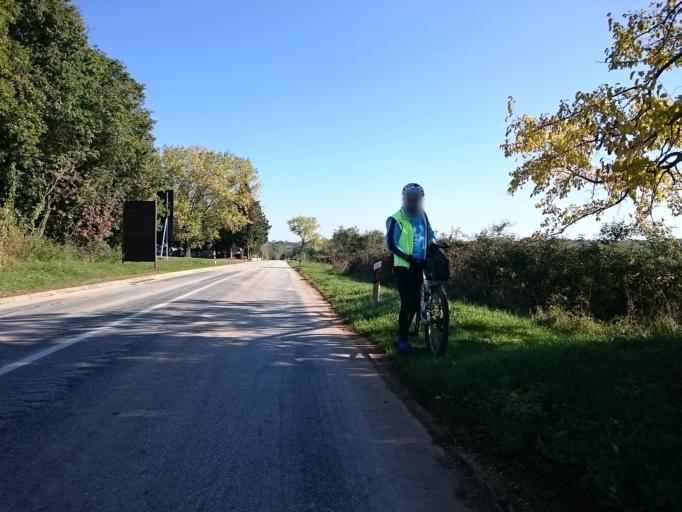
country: HR
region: Istarska
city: Buje
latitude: 45.3671
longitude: 13.6105
